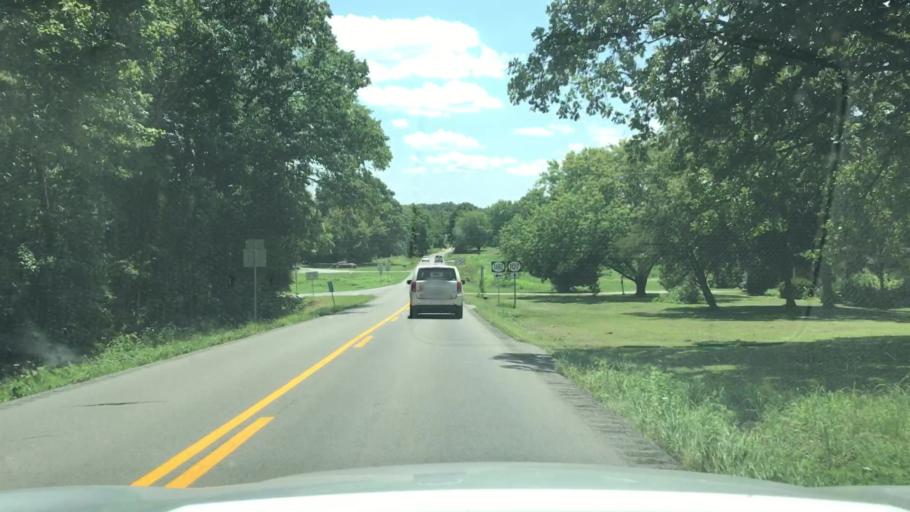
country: US
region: Kentucky
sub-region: Christian County
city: Hopkinsville
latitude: 36.8942
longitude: -87.4523
